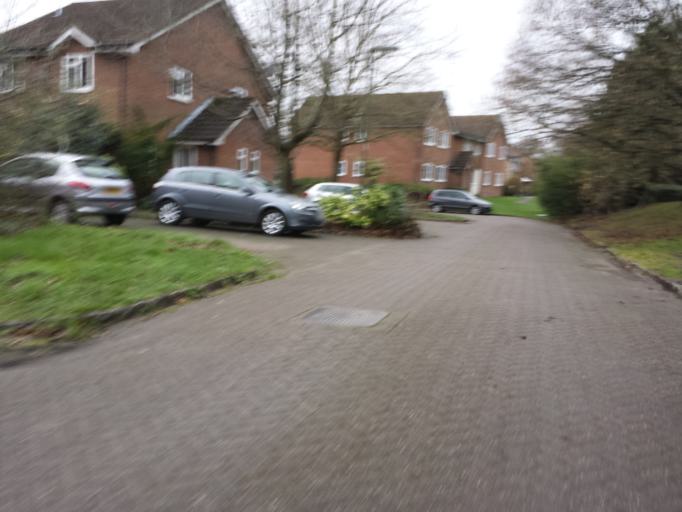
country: GB
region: England
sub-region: Surrey
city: Bagshot
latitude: 51.3539
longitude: -0.6886
